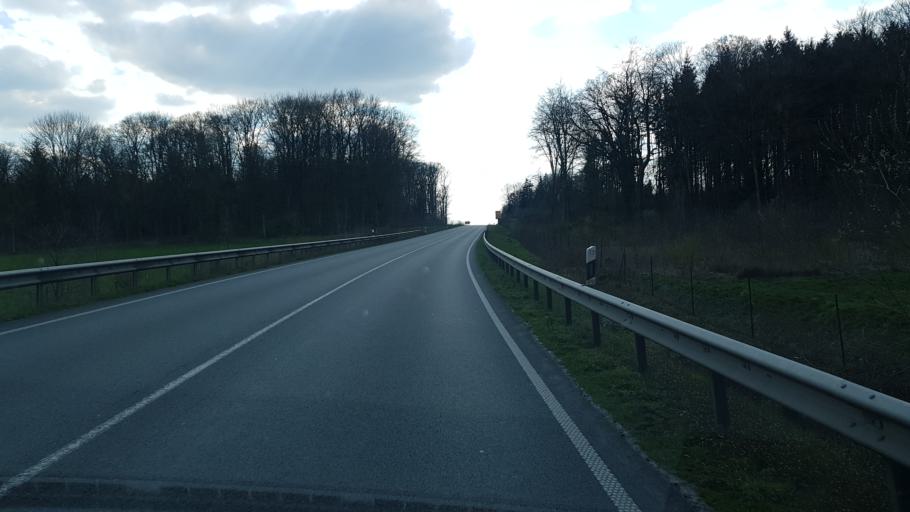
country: DE
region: Lower Saxony
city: Rastede
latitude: 53.2320
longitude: 8.2720
